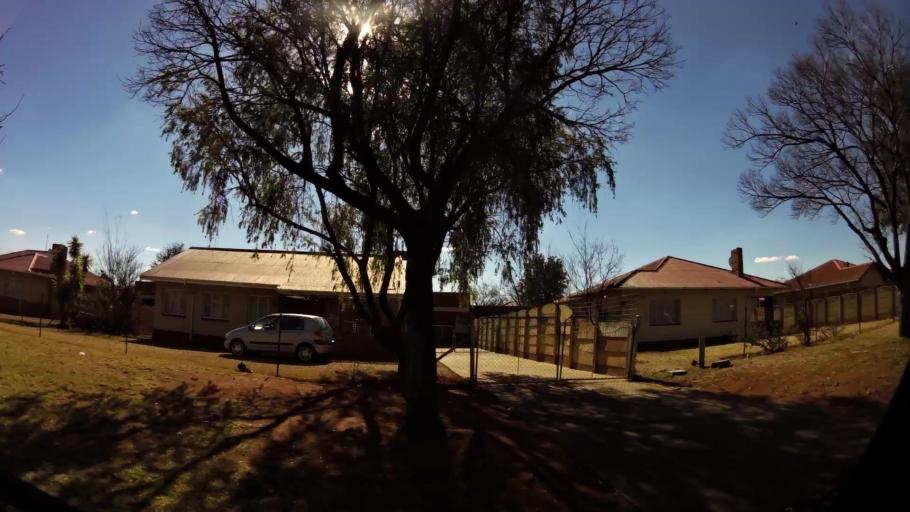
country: ZA
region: Gauteng
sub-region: West Rand District Municipality
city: Carletonville
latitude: -26.3569
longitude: 27.3879
